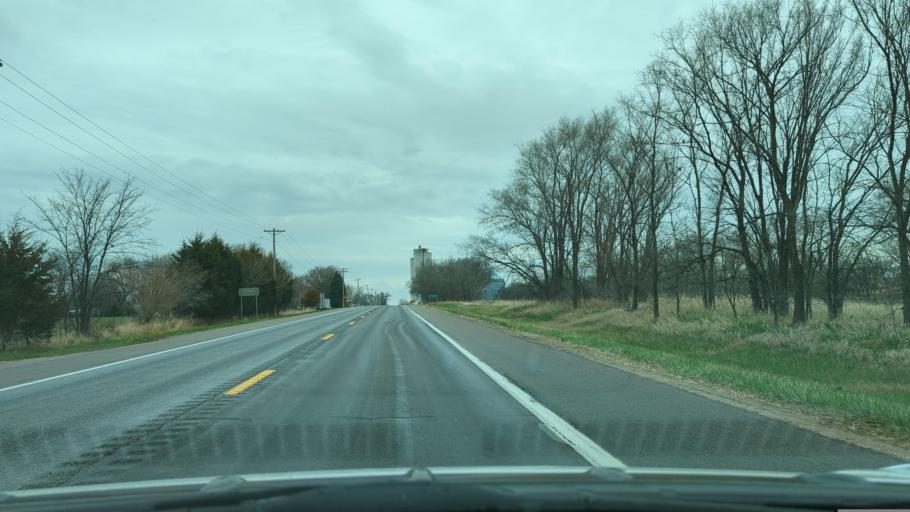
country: US
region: Nebraska
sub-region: Saunders County
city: Ashland
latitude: 40.9670
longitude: -96.4369
